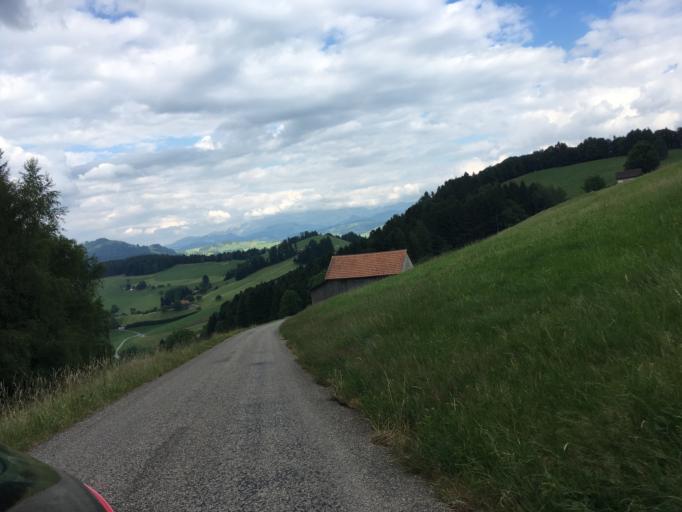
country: CH
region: Saint Gallen
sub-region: Wahlkreis Toggenburg
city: Lichtensteig
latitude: 47.3158
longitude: 9.0429
